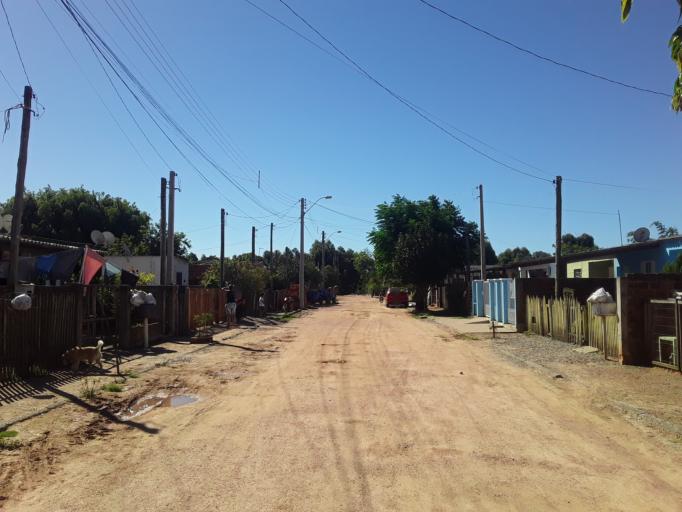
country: BR
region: Rio Grande do Sul
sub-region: Sao Lourenco Do Sul
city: Sao Lourenco do Sul
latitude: -31.3411
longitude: -51.9902
